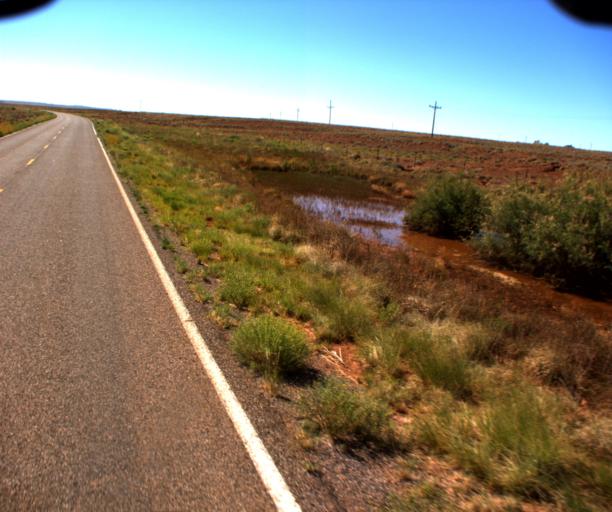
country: US
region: Arizona
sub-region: Coconino County
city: LeChee
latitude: 35.1765
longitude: -110.9255
